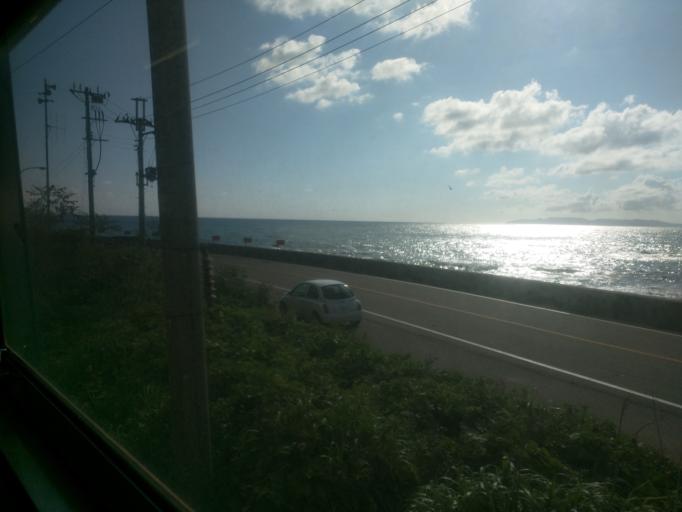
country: JP
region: Niigata
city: Murakami
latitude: 38.4230
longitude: 139.4728
